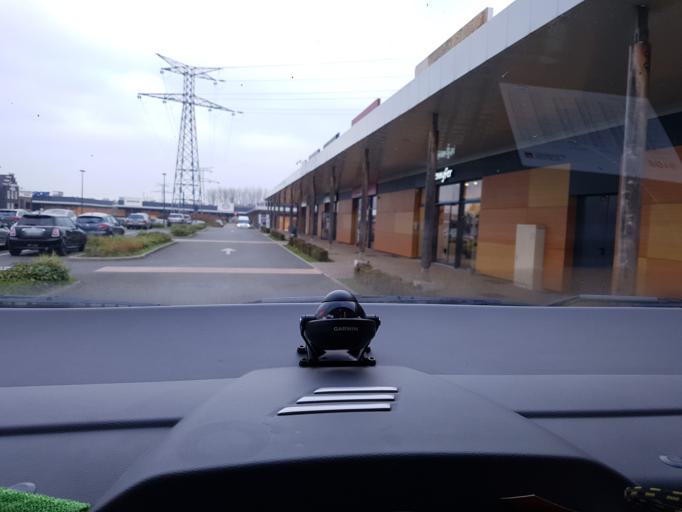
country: FR
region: Haute-Normandie
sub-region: Departement de la Seine-Maritime
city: Eu
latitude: 50.0597
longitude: 1.4078
